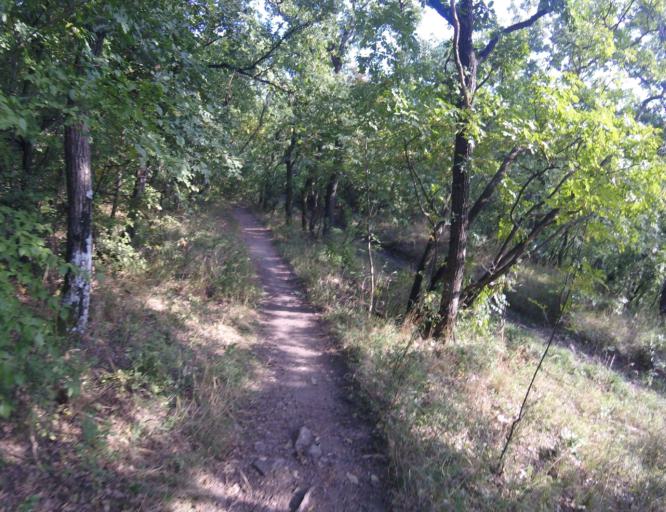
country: HU
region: Pest
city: Nagykovacsi
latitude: 47.6788
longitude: 19.0095
